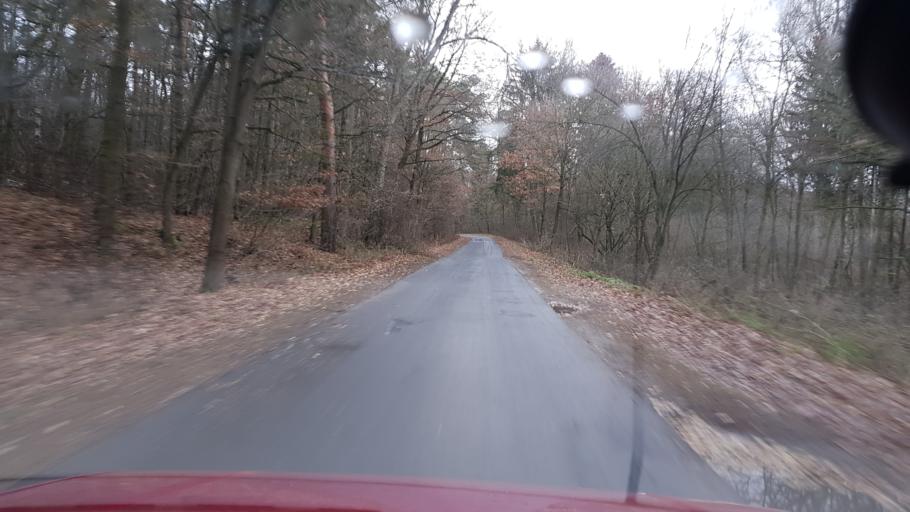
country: PL
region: West Pomeranian Voivodeship
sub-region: Powiat stargardzki
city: Stargard Szczecinski
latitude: 53.3277
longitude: 15.1259
